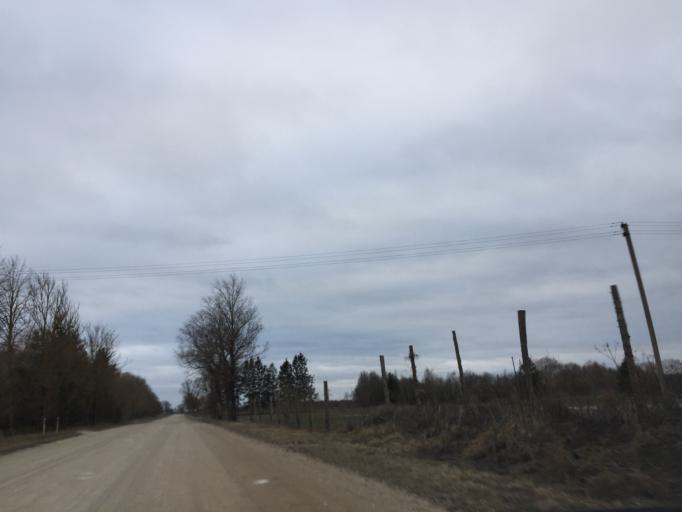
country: LT
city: Zagare
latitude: 56.3520
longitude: 23.2549
